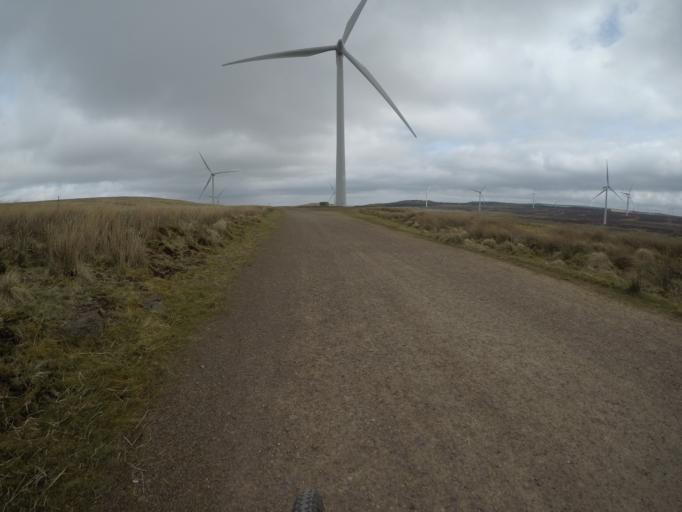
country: GB
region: Scotland
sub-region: East Renfrewshire
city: Eaglesham
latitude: 55.7039
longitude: -4.3189
